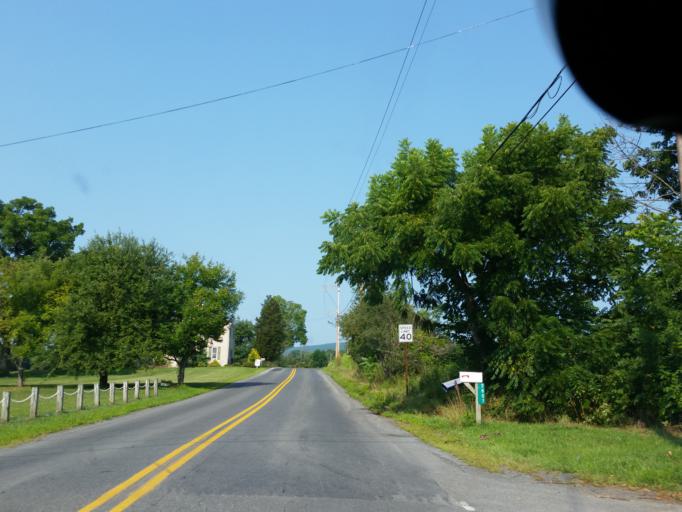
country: US
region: Pennsylvania
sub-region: Union County
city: New Columbia
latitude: 41.0529
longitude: -76.9031
